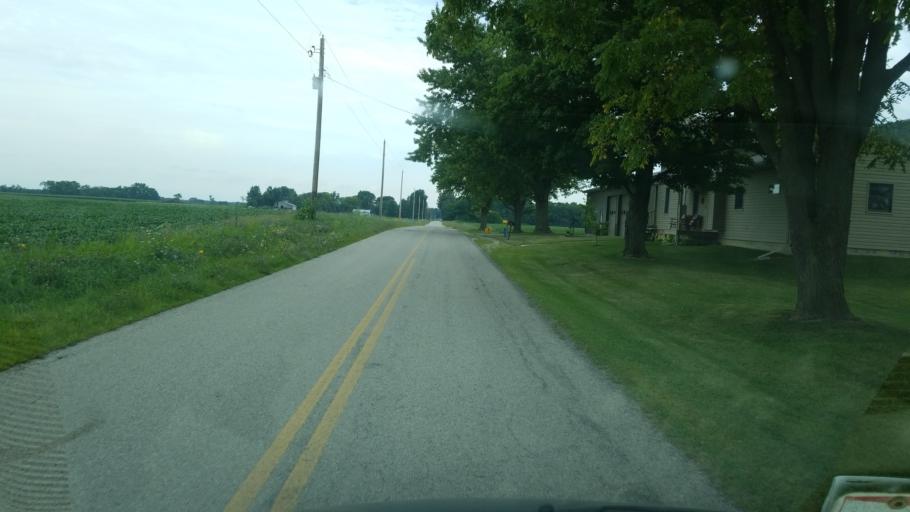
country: US
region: Ohio
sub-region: Seneca County
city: Tiffin
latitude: 41.0087
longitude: -83.0546
